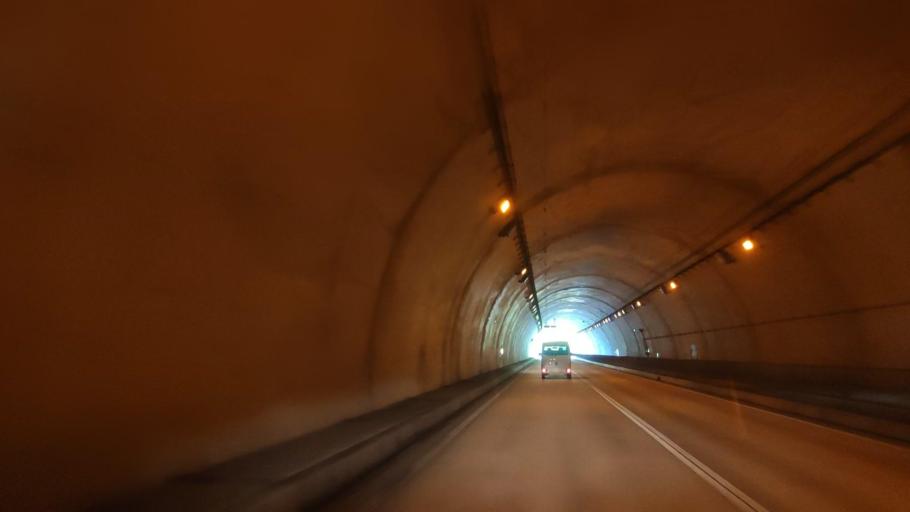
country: JP
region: Hyogo
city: Toyooka
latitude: 35.4910
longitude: 134.6200
